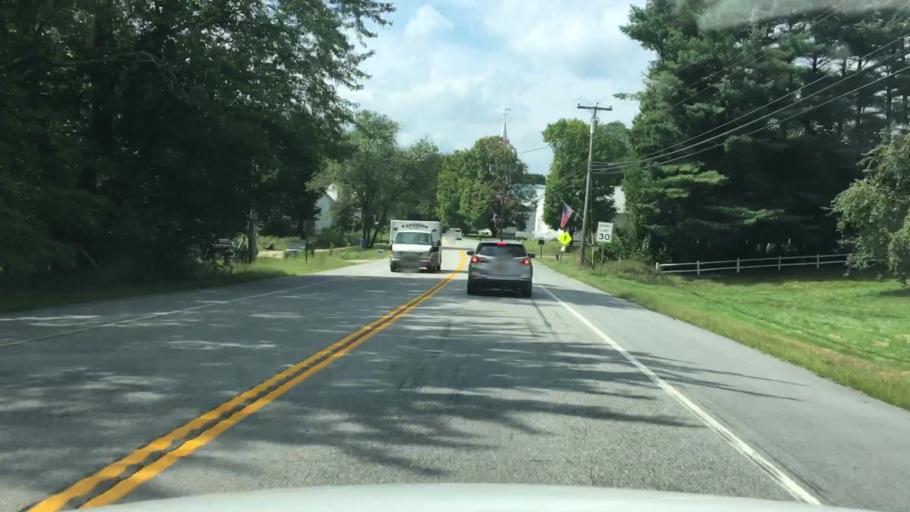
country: US
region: Maine
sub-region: Oxford County
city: Rumford
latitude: 44.5125
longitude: -70.6117
